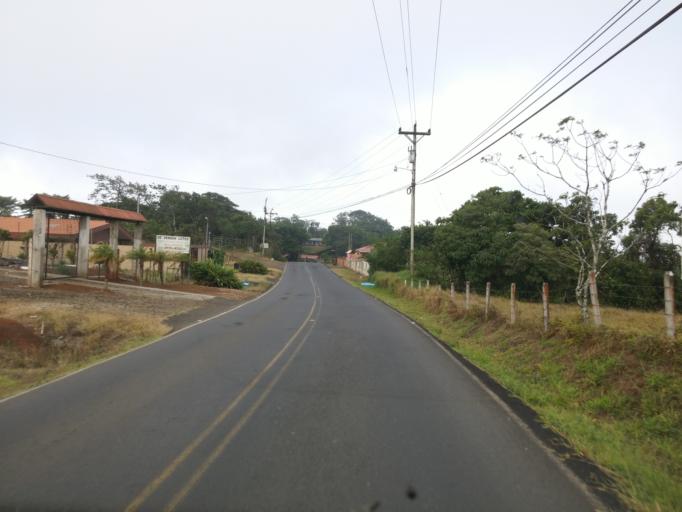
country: CR
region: Alajuela
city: San Ramon
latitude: 10.1415
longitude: -84.4805
